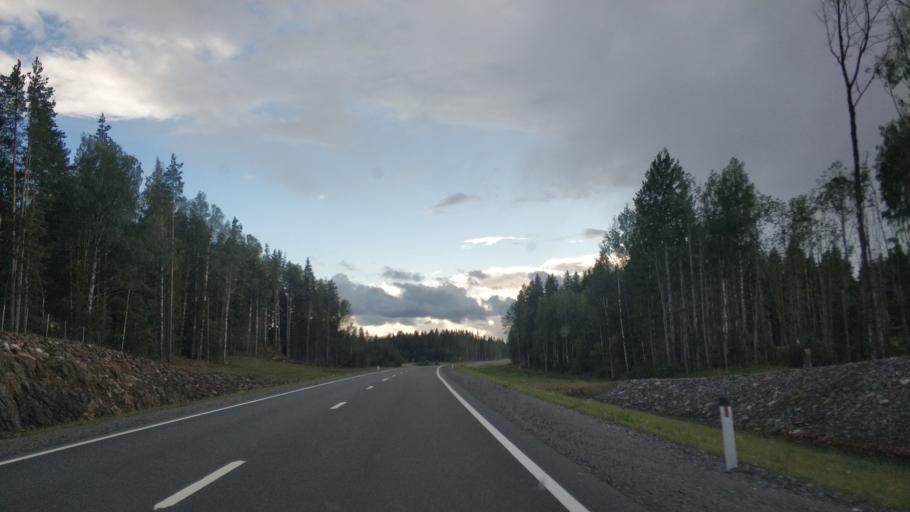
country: RU
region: Republic of Karelia
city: Lakhdenpokh'ya
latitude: 61.4571
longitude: 29.9985
